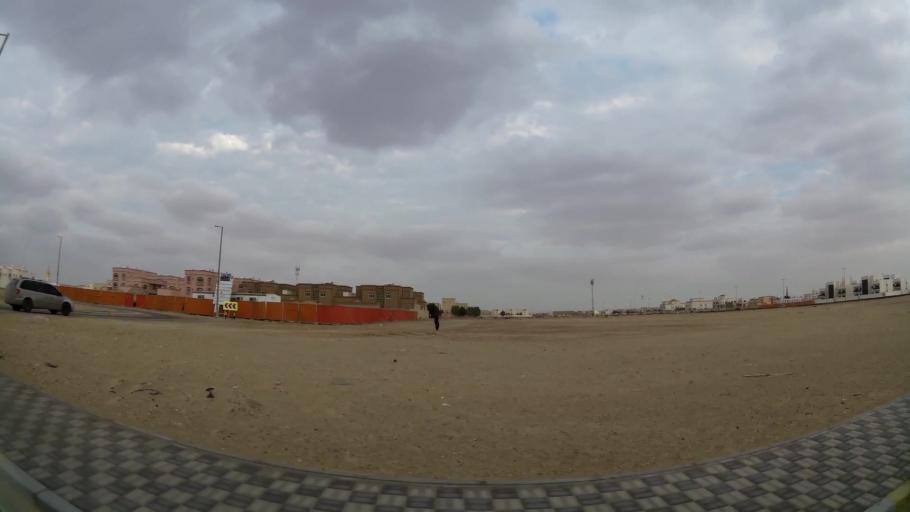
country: AE
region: Abu Dhabi
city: Abu Dhabi
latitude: 24.3489
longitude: 54.5430
